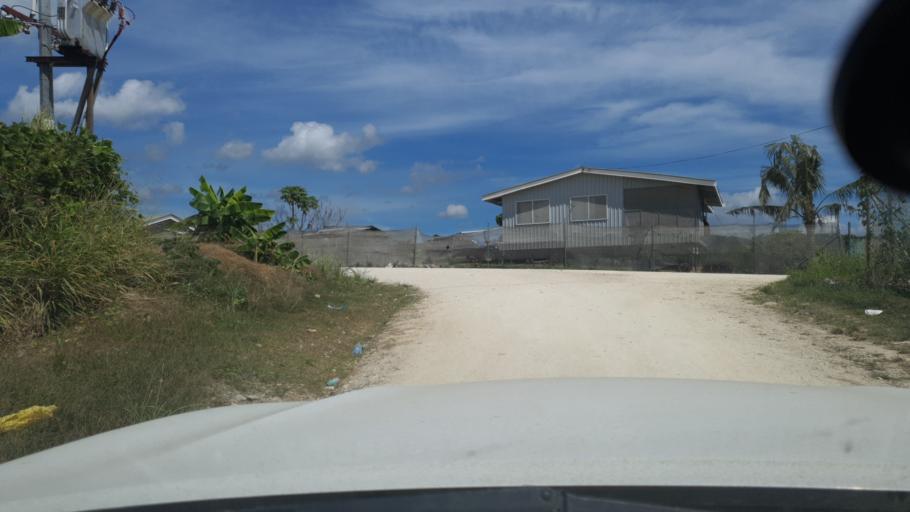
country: SB
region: Guadalcanal
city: Honiara
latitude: -9.4330
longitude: 159.9264
